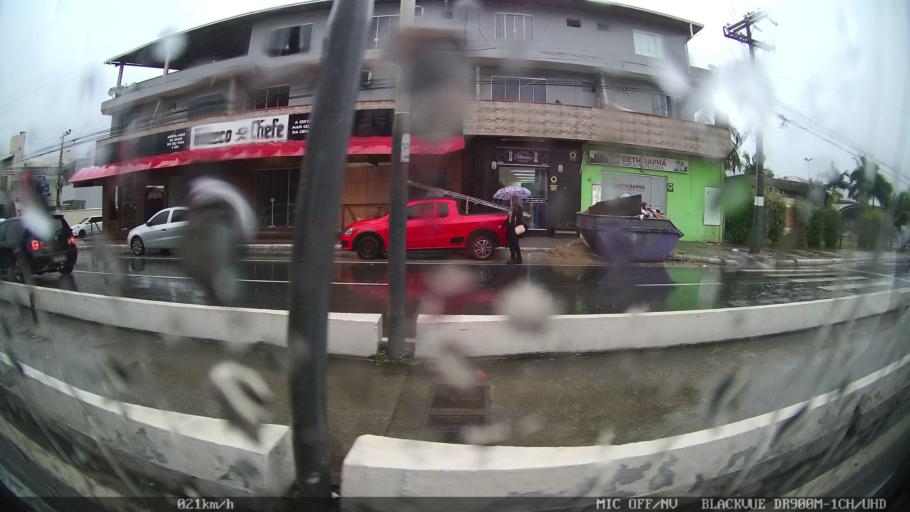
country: BR
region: Santa Catarina
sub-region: Balneario Camboriu
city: Balneario Camboriu
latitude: -27.0051
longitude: -48.6335
